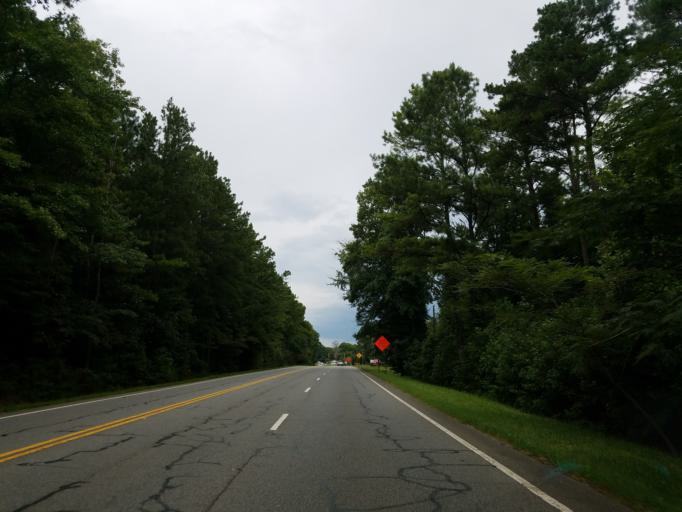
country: US
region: Georgia
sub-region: Bartow County
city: Adairsville
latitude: 34.2793
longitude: -84.8684
